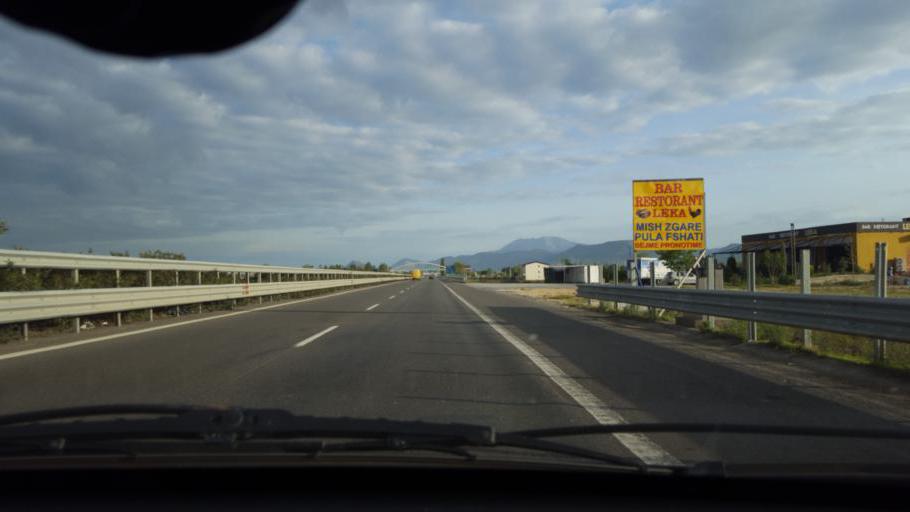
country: AL
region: Lezhe
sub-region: Rrethi i Kurbinit
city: Lac
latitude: 41.6466
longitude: 19.6714
